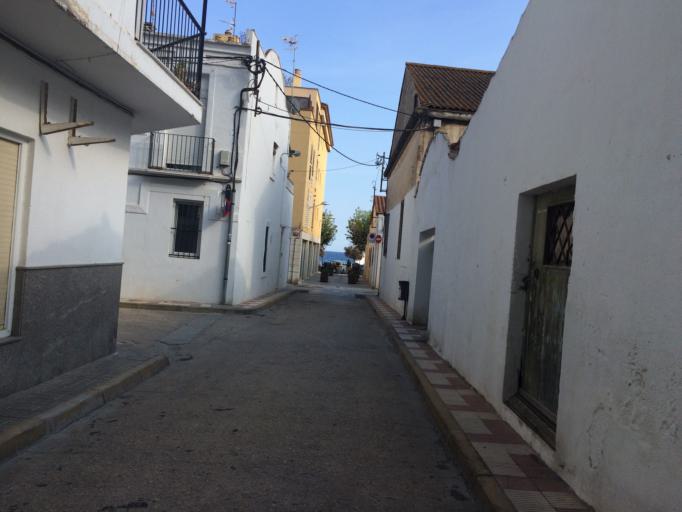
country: ES
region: Catalonia
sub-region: Provincia de Girona
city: Blanes
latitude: 41.6712
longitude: 2.7885
